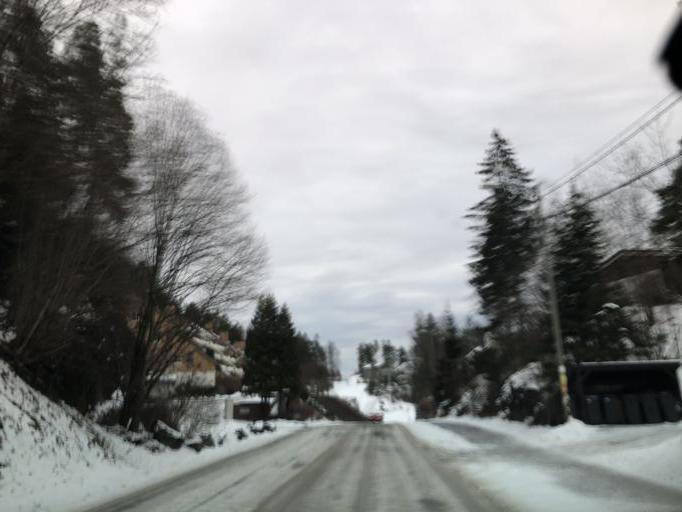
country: NO
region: Akershus
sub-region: Baerum
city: Sandvika
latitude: 59.8677
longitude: 10.5139
